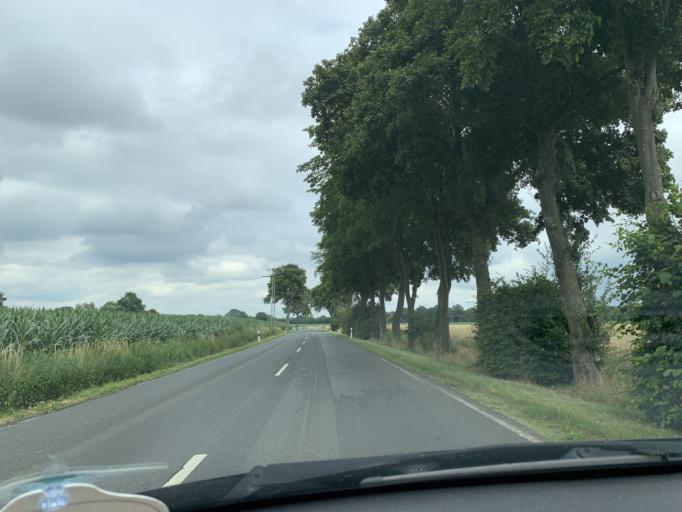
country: DE
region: North Rhine-Westphalia
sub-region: Regierungsbezirk Munster
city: Wadersloh
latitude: 51.7125
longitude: 8.2974
